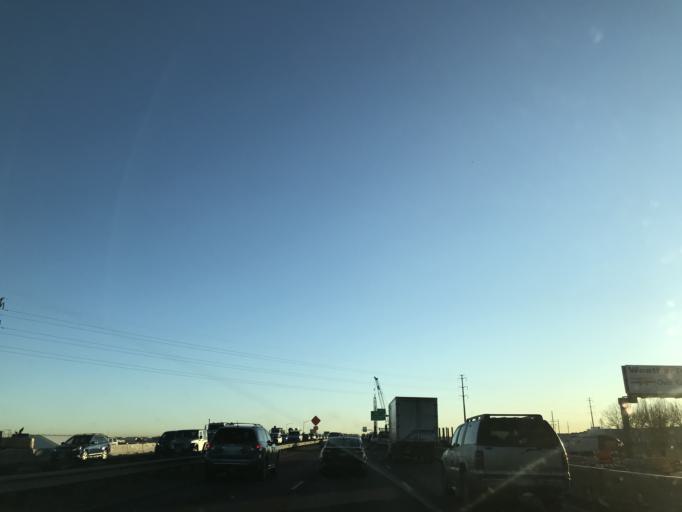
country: US
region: Colorado
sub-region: Adams County
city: Commerce City
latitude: 39.7782
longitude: -104.9095
